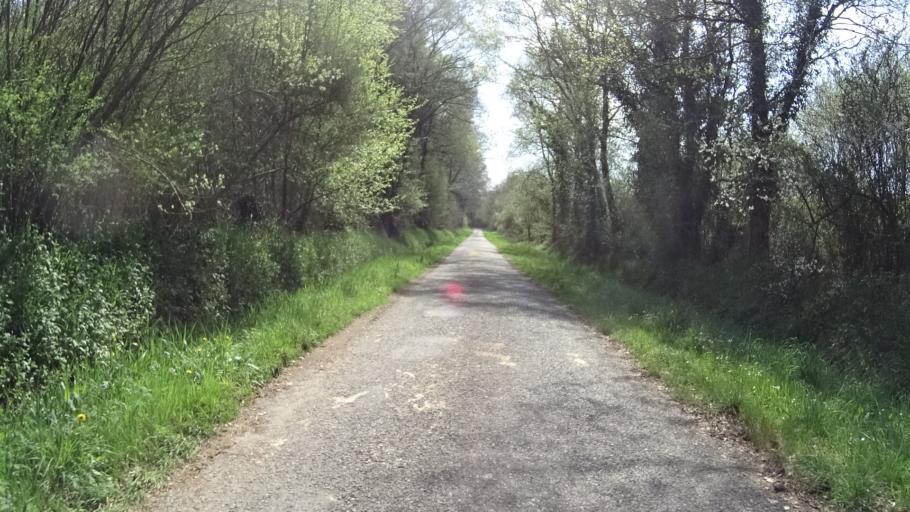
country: FR
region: Brittany
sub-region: Departement du Finistere
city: Sizun
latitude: 48.4326
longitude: -4.1032
